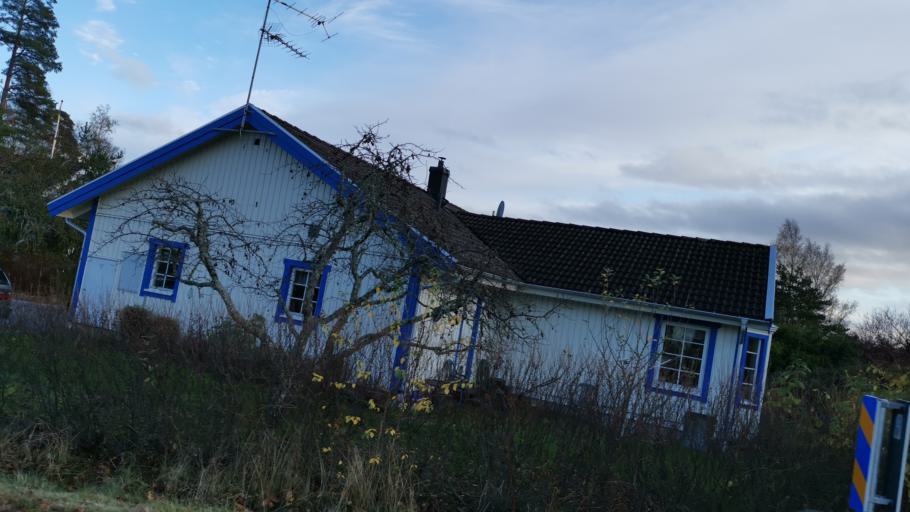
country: SE
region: Vaestra Goetaland
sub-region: Munkedals Kommun
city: Munkedal
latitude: 58.4619
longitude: 11.6655
